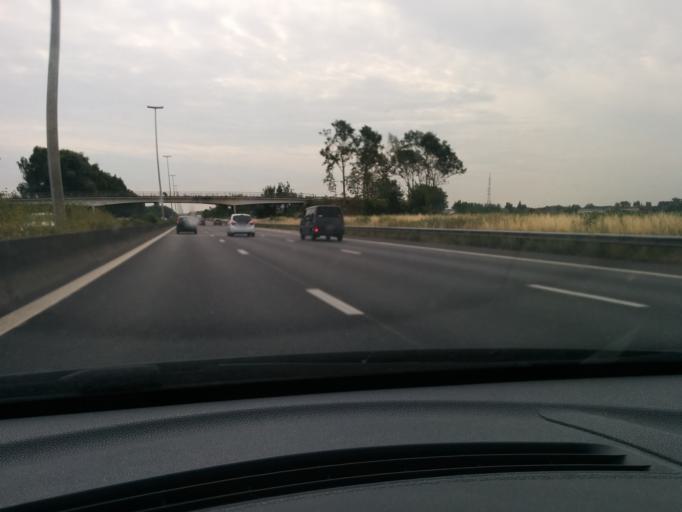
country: BE
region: Flanders
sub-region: Provincie Oost-Vlaanderen
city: Nevele
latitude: 51.0471
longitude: 3.5853
